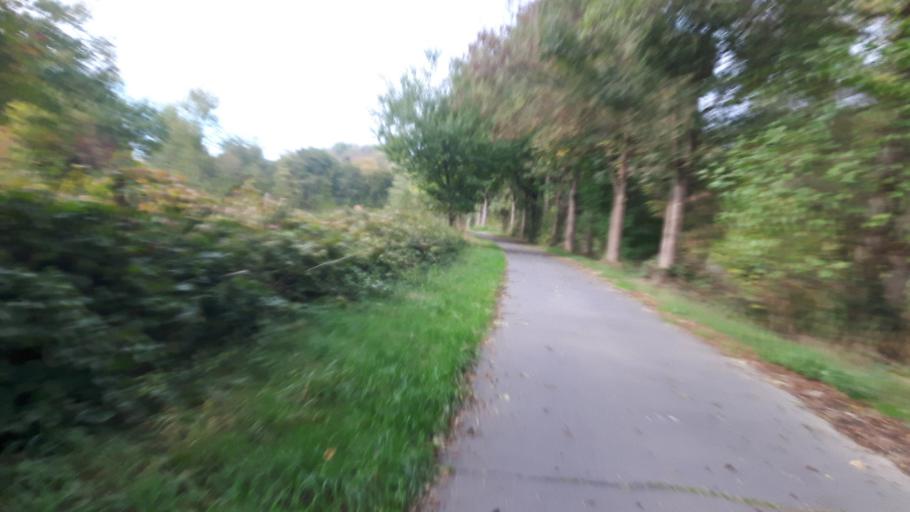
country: DE
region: Rheinland-Pfalz
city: Werkhausen
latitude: 50.7689
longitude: 7.5247
